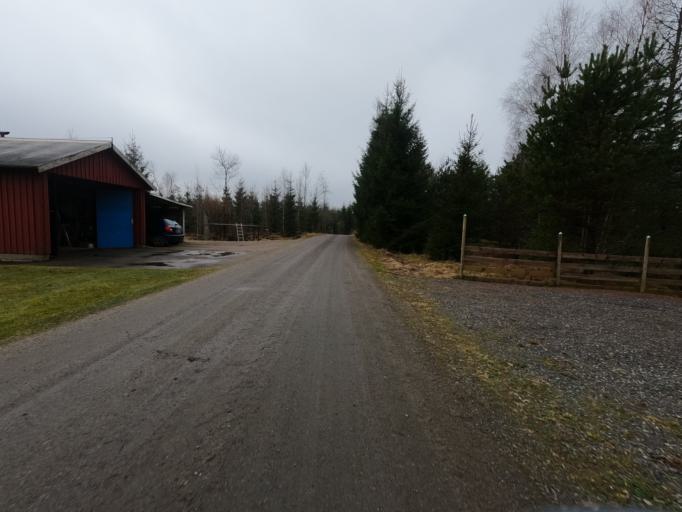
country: SE
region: Kronoberg
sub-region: Markaryds Kommun
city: Stromsnasbruk
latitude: 56.7997
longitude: 13.5600
